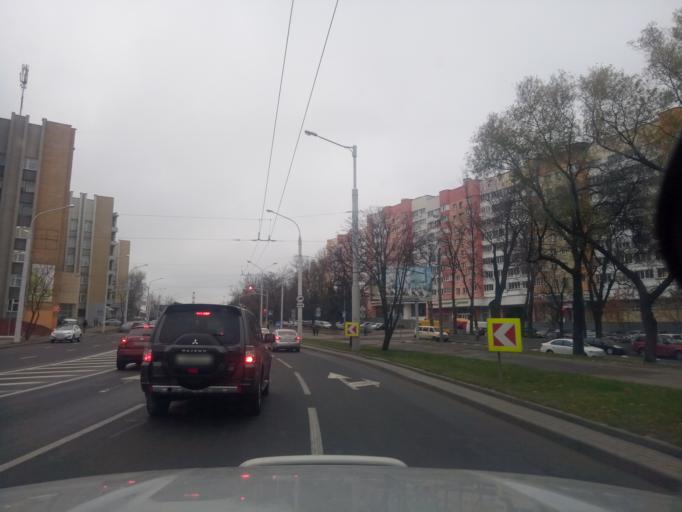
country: BY
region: Minsk
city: Minsk
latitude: 53.9074
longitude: 27.5332
